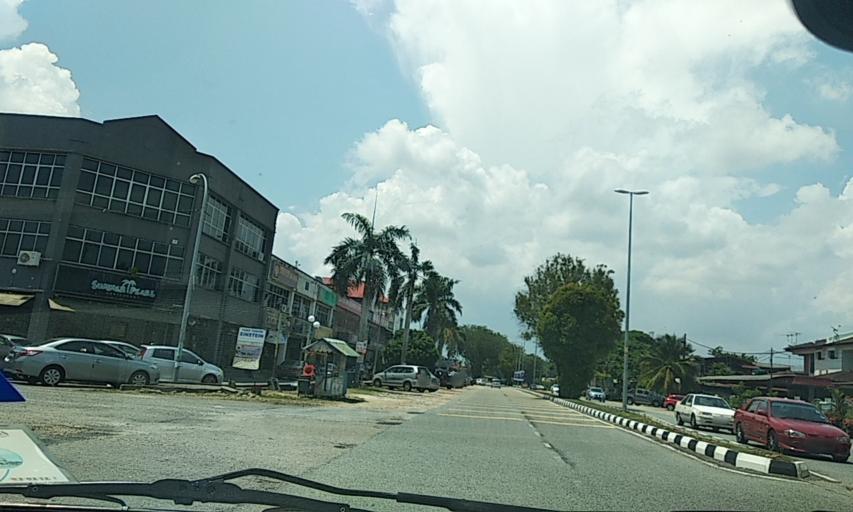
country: MY
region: Kedah
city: Sungai Petani
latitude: 5.6364
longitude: 100.4722
